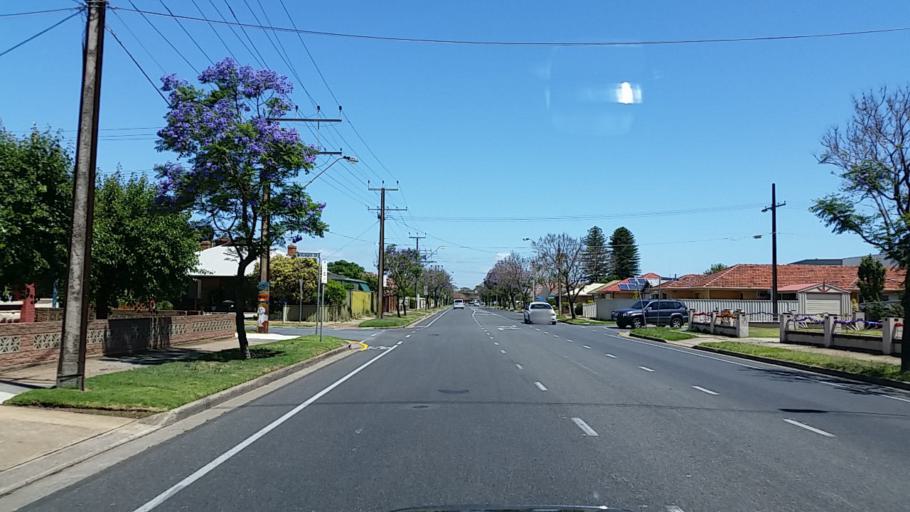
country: AU
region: South Australia
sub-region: Charles Sturt
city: Allenby Gardens
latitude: -34.9006
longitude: 138.5518
